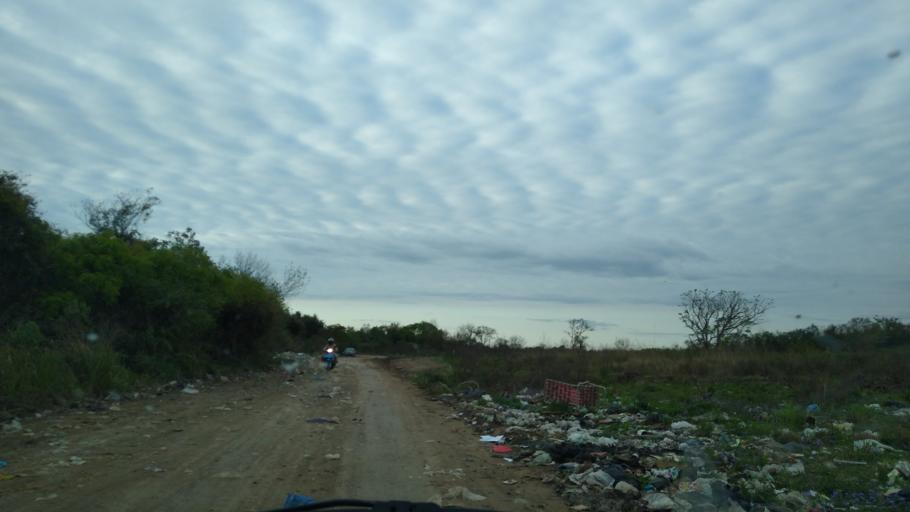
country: AR
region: Chaco
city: Fontana
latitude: -27.3949
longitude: -59.0495
